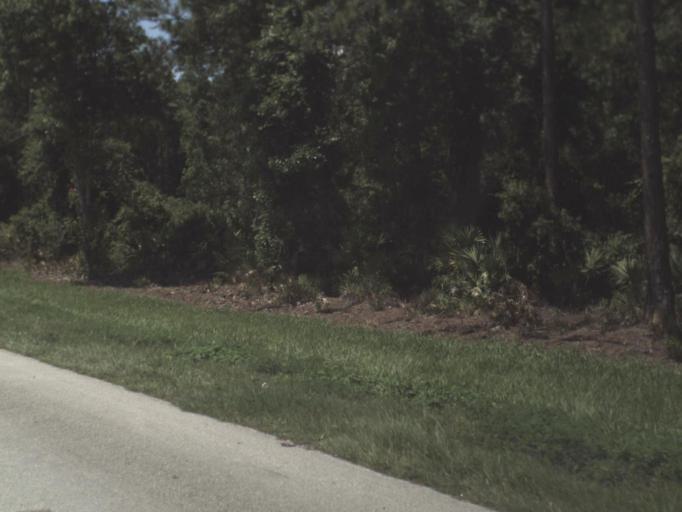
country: US
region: Florida
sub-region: Saint Johns County
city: Saint Augustine South
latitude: 29.8457
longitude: -81.3893
